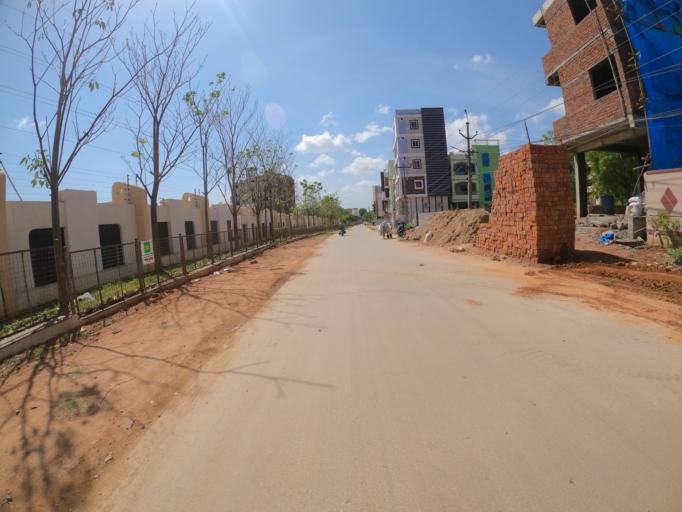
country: IN
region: Telangana
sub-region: Hyderabad
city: Hyderabad
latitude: 17.3590
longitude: 78.3807
